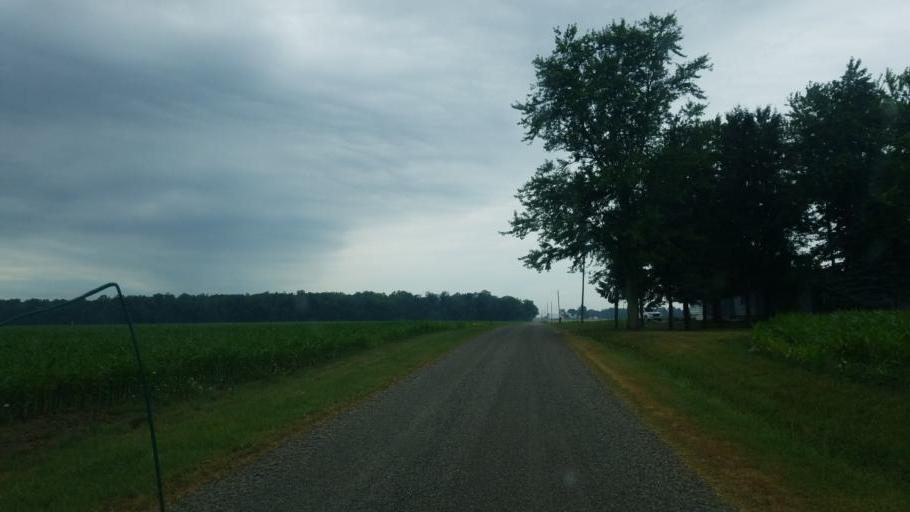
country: US
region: Indiana
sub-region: DeKalb County
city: Butler
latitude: 41.4607
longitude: -84.9100
